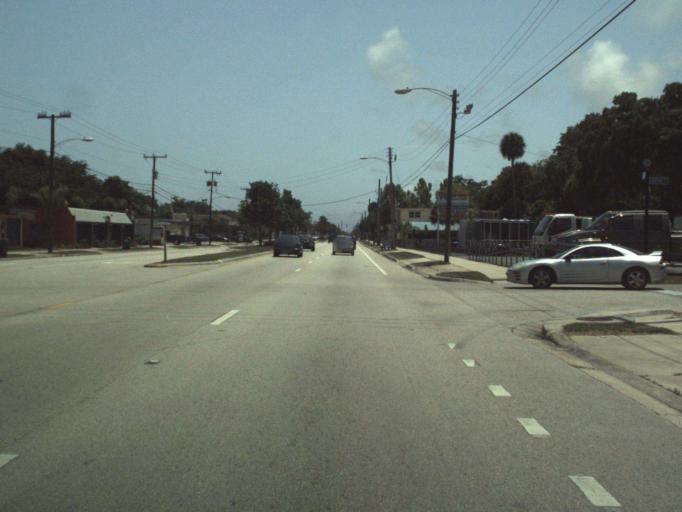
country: US
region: Florida
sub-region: Volusia County
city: Holly Hill
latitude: 29.2427
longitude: -81.0401
